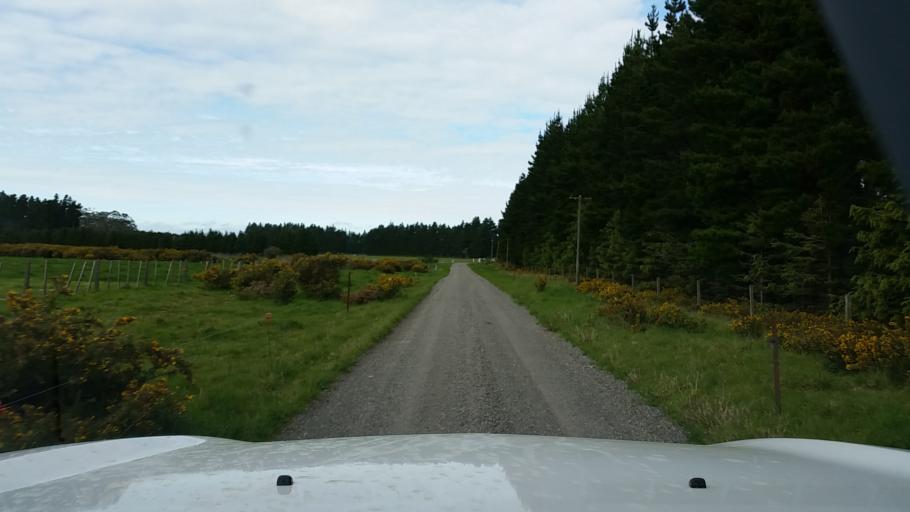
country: NZ
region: Wellington
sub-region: Upper Hutt City
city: Upper Hutt
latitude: -41.0913
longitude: 175.3542
